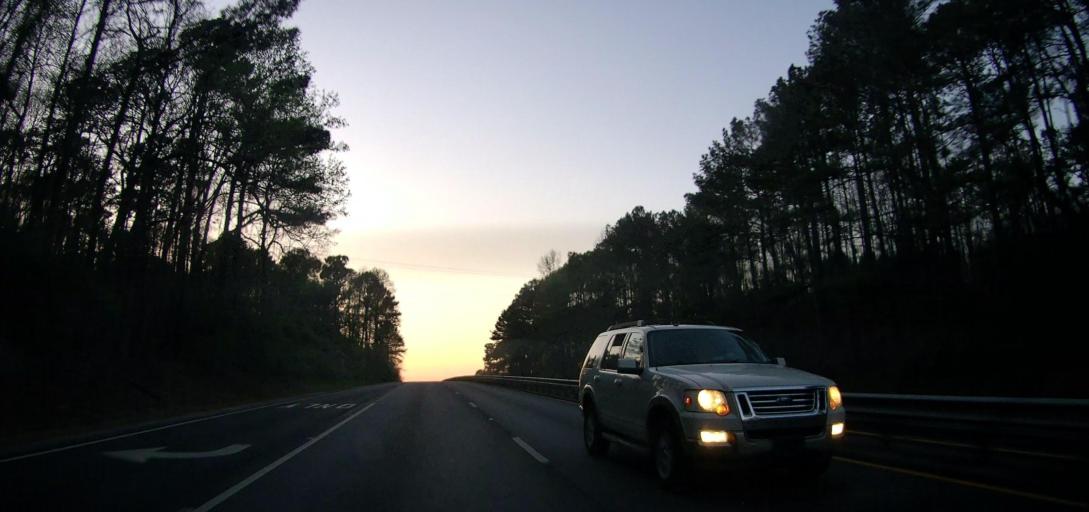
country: US
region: Alabama
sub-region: Tallapoosa County
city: Alexander City
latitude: 32.9031
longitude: -85.8941
